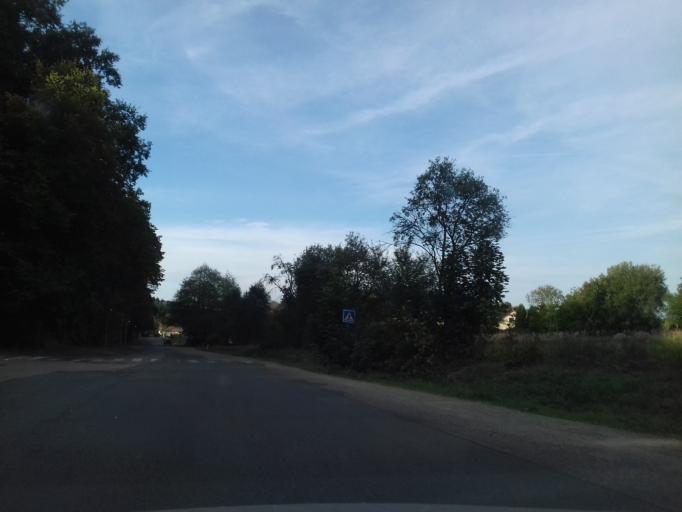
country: CZ
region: Central Bohemia
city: Neveklov
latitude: 49.7563
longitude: 14.5297
